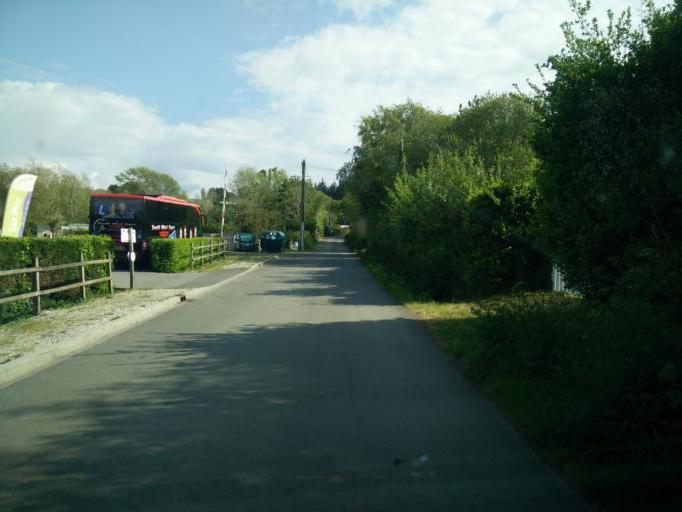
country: FR
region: Brittany
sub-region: Departement du Finistere
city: Crozon
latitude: 48.2389
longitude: -4.5448
